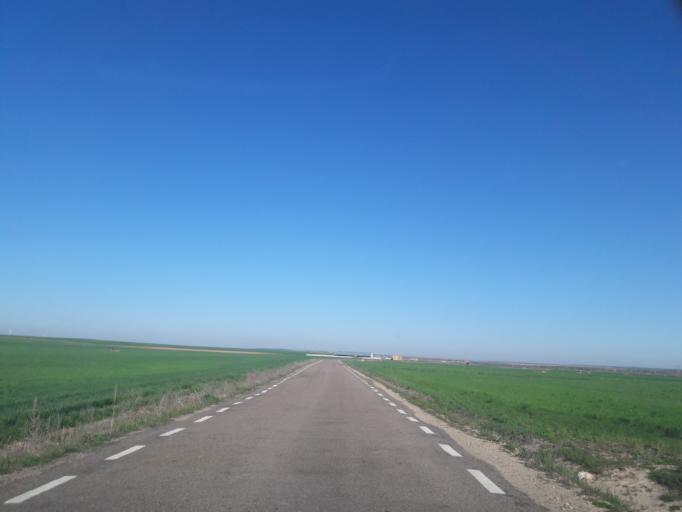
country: ES
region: Castille and Leon
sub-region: Provincia de Salamanca
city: Coca de Alba
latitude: 40.8626
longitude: -5.3681
